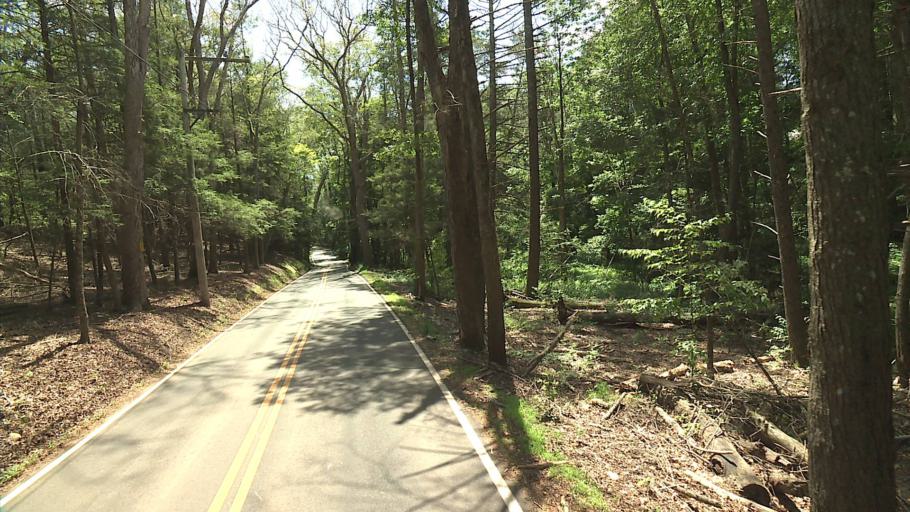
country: US
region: Connecticut
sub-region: Middlesex County
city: Essex Village
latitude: 41.4544
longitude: -72.3386
